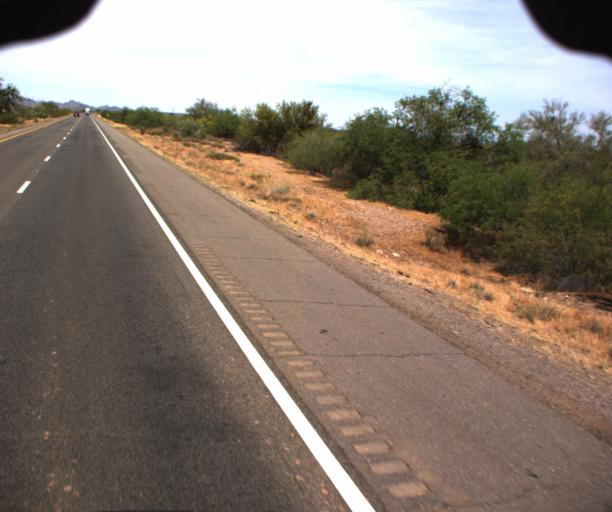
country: US
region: Arizona
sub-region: Maricopa County
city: Wickenburg
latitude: 33.8351
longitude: -112.6036
